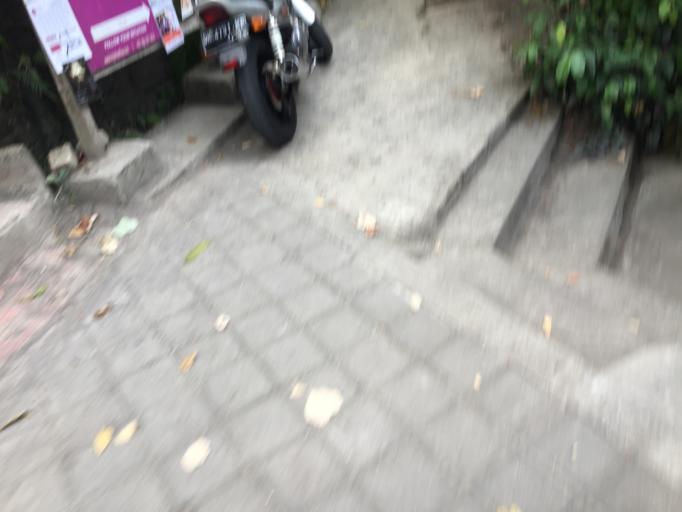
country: ID
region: Bali
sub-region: Kabupaten Gianyar
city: Ubud
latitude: -8.5033
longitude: 115.2520
